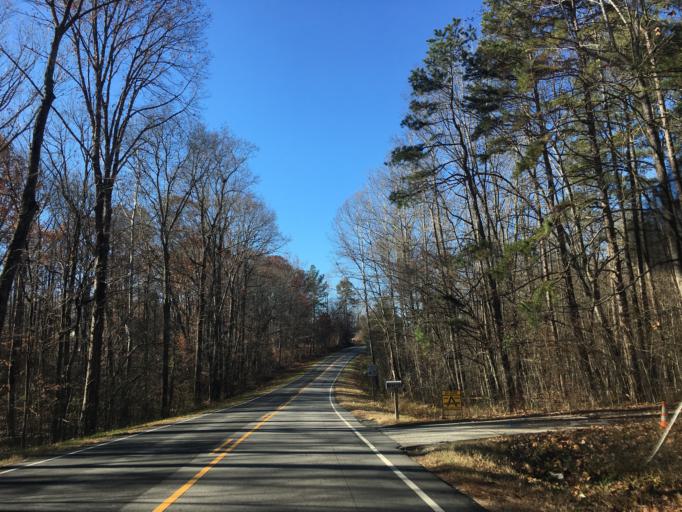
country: US
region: North Carolina
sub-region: Rowan County
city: Salisbury
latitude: 35.6384
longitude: -80.5380
